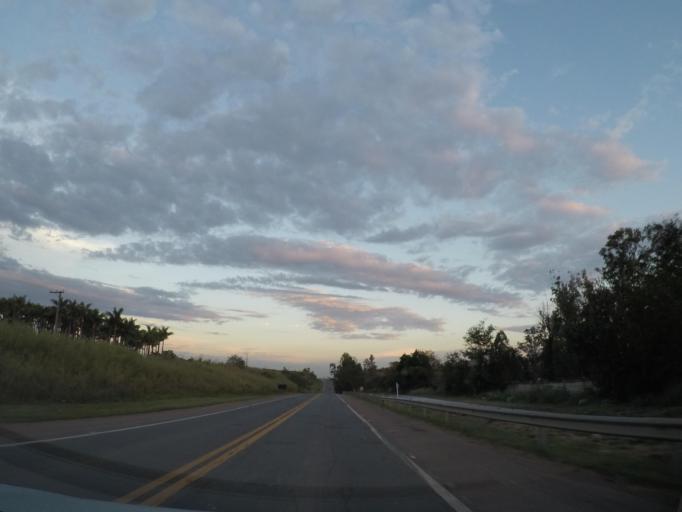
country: BR
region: Sao Paulo
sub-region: Vinhedo
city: Vinhedo
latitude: -23.0512
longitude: -47.0754
